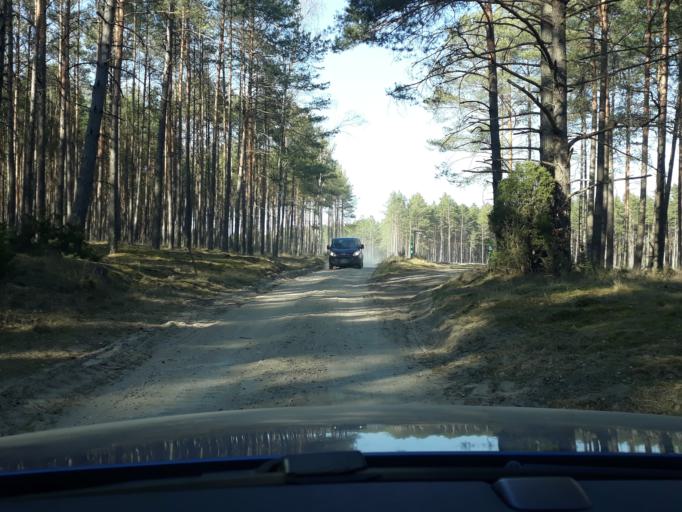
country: PL
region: Pomeranian Voivodeship
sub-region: Powiat bytowski
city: Lipnica
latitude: 53.9139
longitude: 17.4359
